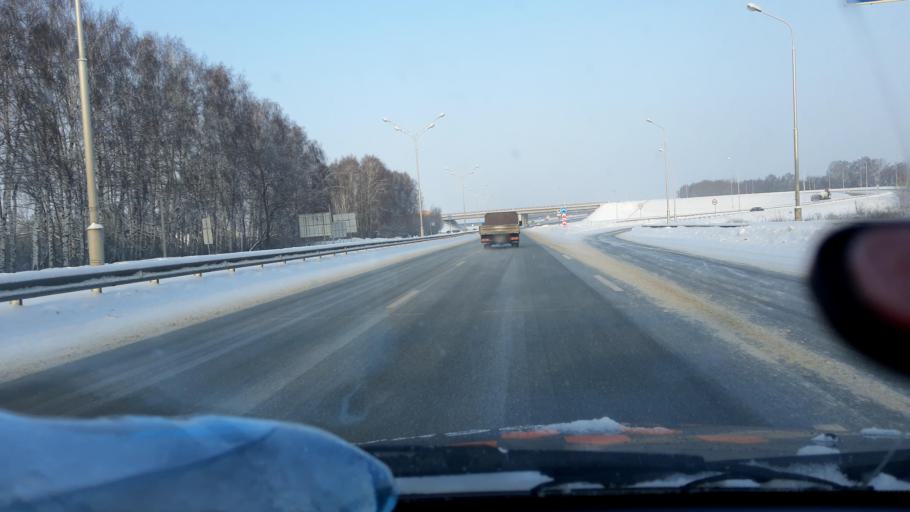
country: RU
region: Bashkortostan
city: Ufa
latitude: 54.5705
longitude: 55.9123
